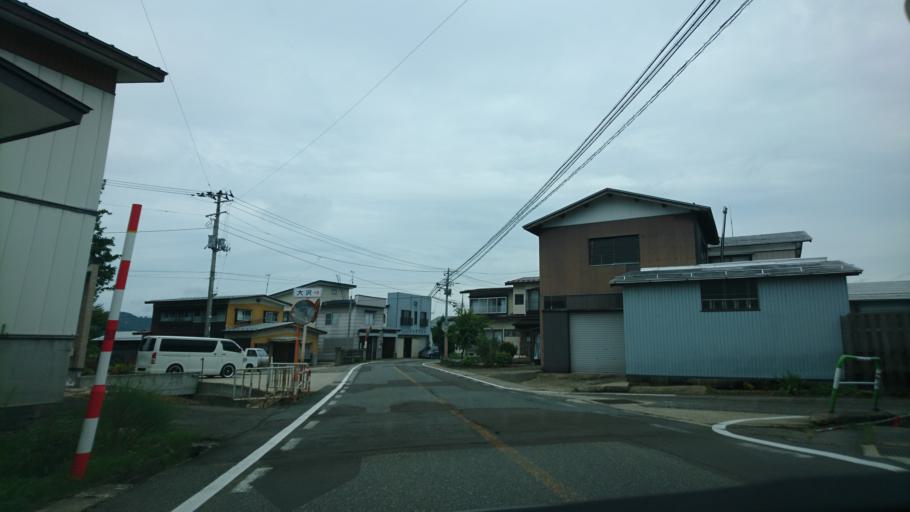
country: JP
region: Akita
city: Yuzawa
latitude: 39.1321
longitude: 140.5758
